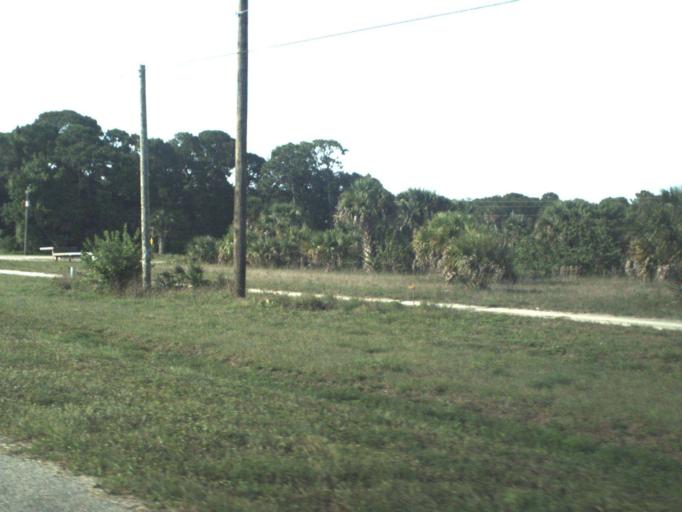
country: US
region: Florida
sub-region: Volusia County
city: Oak Hill
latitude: 28.8994
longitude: -80.8629
